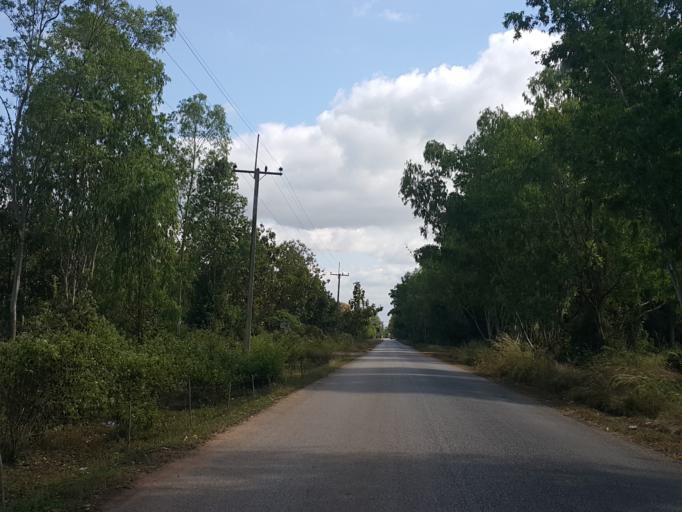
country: TH
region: Lampang
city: Hang Chat
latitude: 18.3496
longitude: 99.3718
